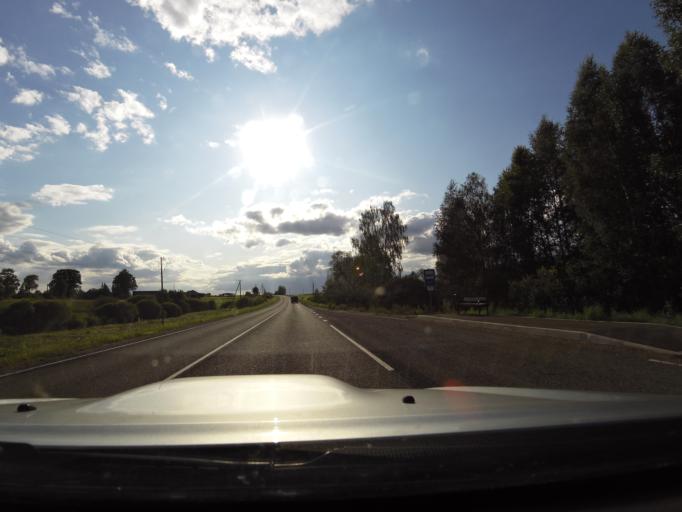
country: LV
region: Viesite
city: Viesite
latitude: 56.1995
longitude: 25.5071
